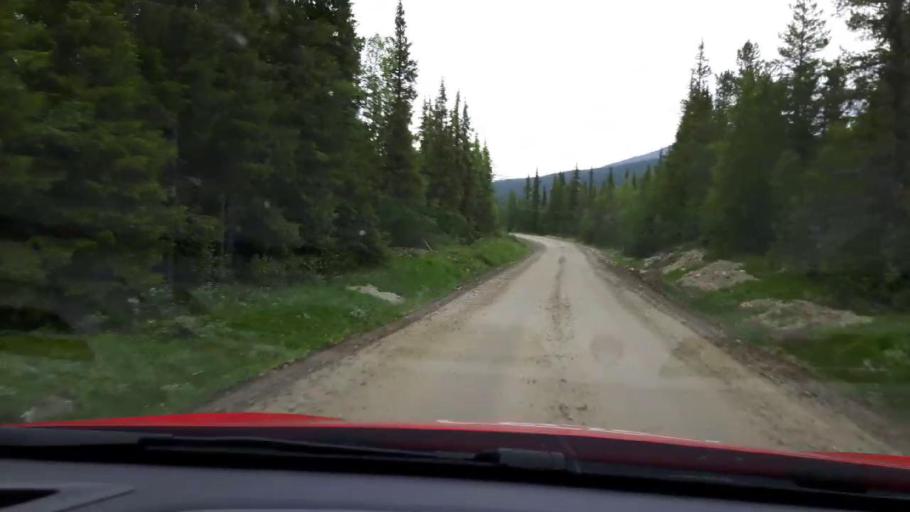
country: SE
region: Jaemtland
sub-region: Are Kommun
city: Are
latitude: 62.8524
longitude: 12.7942
